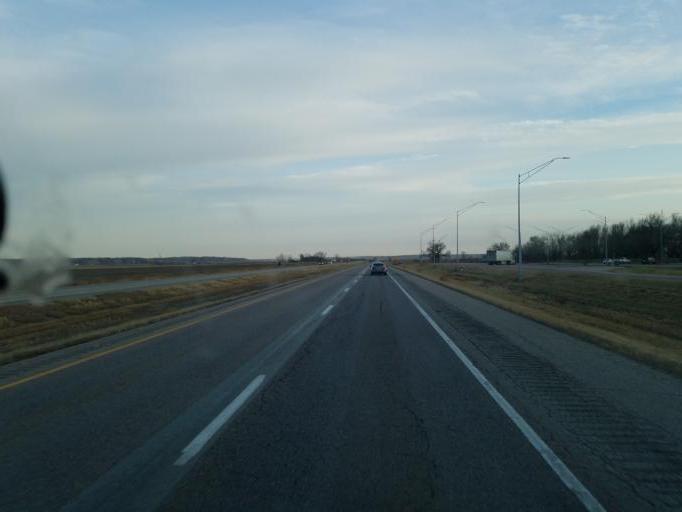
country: US
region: Iowa
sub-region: Harrison County
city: Missouri Valley
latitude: 41.5930
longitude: -95.9541
